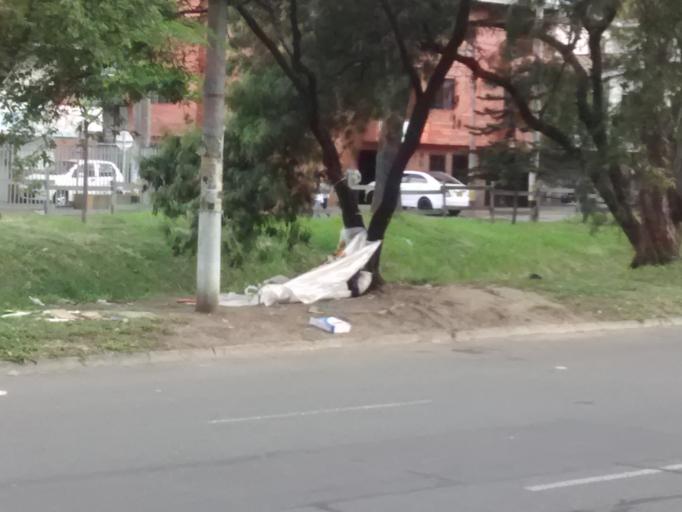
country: CO
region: Antioquia
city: Medellin
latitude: 6.2241
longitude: -75.5842
